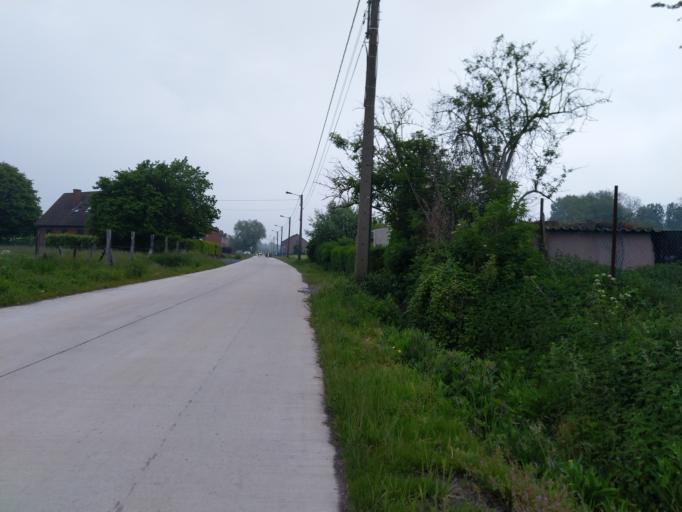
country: BE
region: Wallonia
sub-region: Province du Hainaut
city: Quaregnon
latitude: 50.4603
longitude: 3.9055
